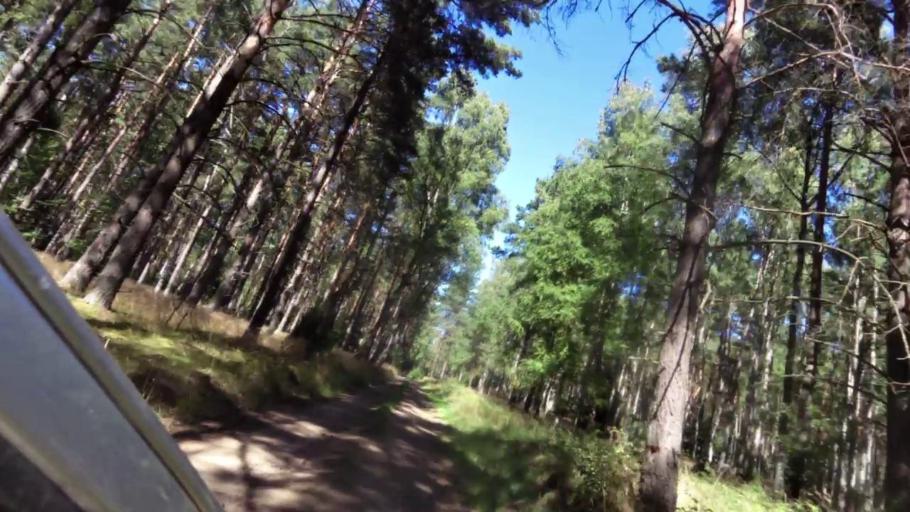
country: PL
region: West Pomeranian Voivodeship
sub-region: Powiat szczecinecki
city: Bialy Bor
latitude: 53.8201
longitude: 16.8633
